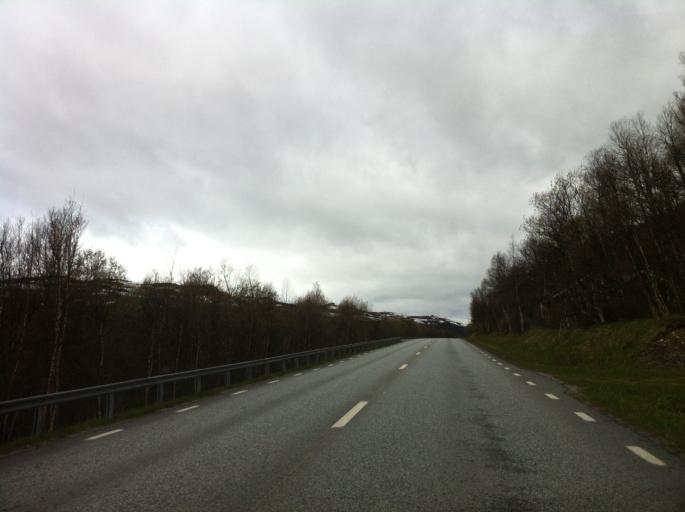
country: NO
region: Sor-Trondelag
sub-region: Tydal
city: Aas
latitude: 62.5505
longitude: 12.3033
